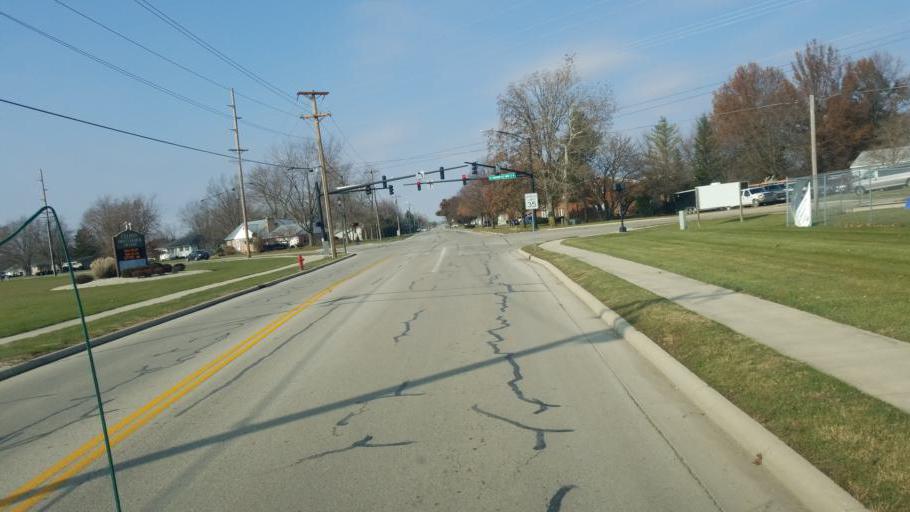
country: US
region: Ohio
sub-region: Mercer County
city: Celina
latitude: 40.5599
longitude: -84.5802
